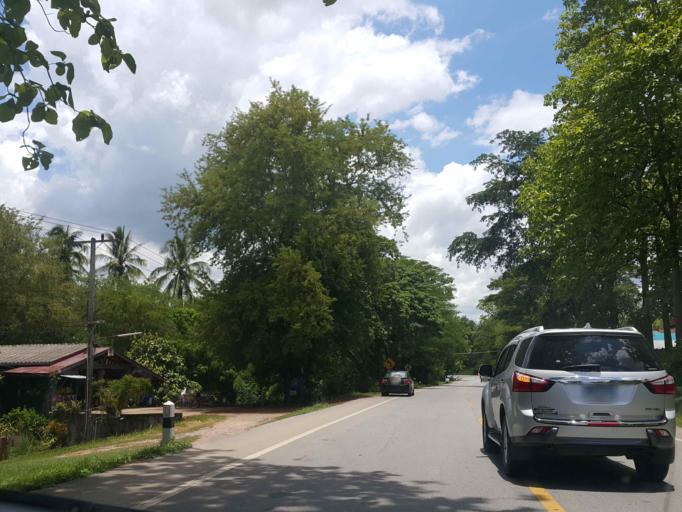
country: TH
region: Nan
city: Wiang Sa
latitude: 18.5164
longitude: 100.5976
